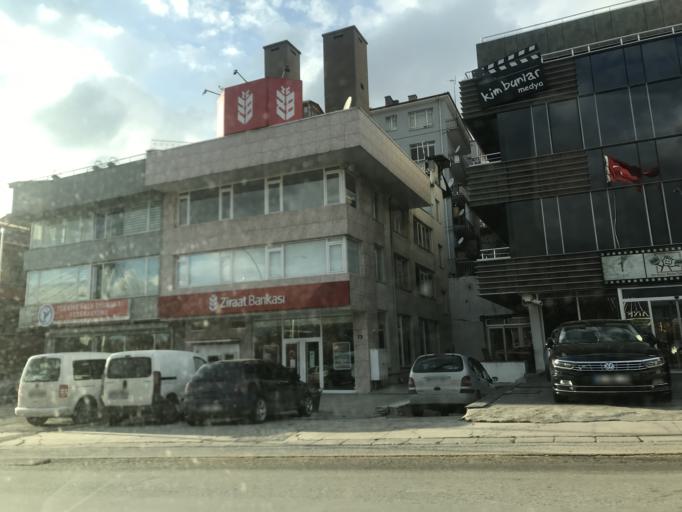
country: TR
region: Ankara
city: Mamak
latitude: 39.9674
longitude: 32.8744
